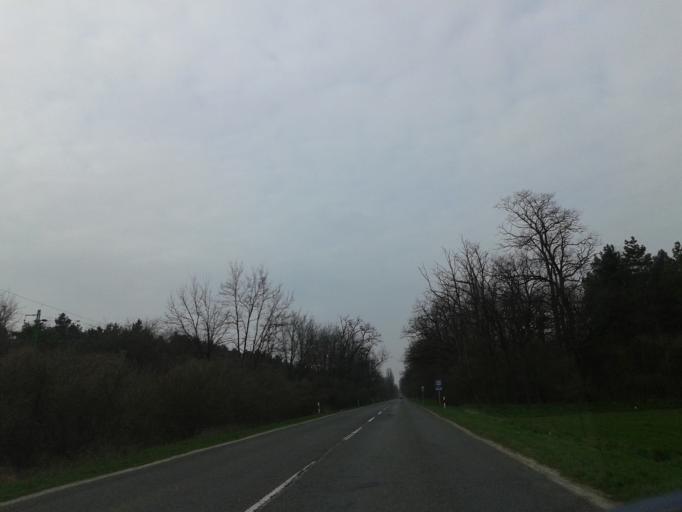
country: HU
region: Komarom-Esztergom
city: Acs
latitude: 47.7300
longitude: 18.0573
